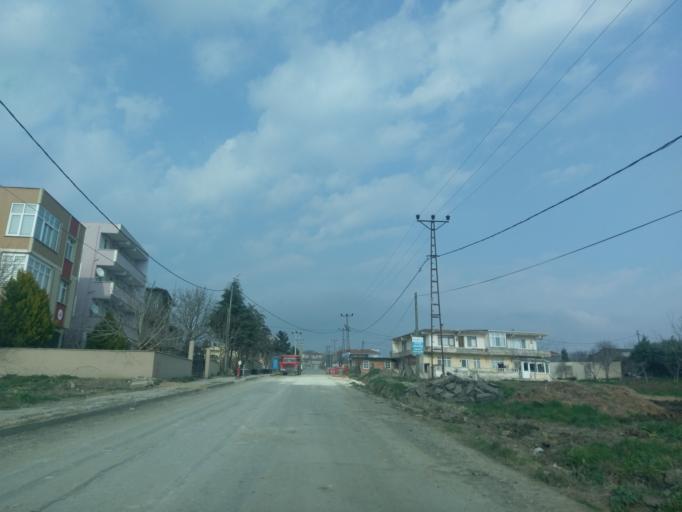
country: TR
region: Istanbul
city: Kavakli
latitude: 41.1249
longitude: 28.3190
